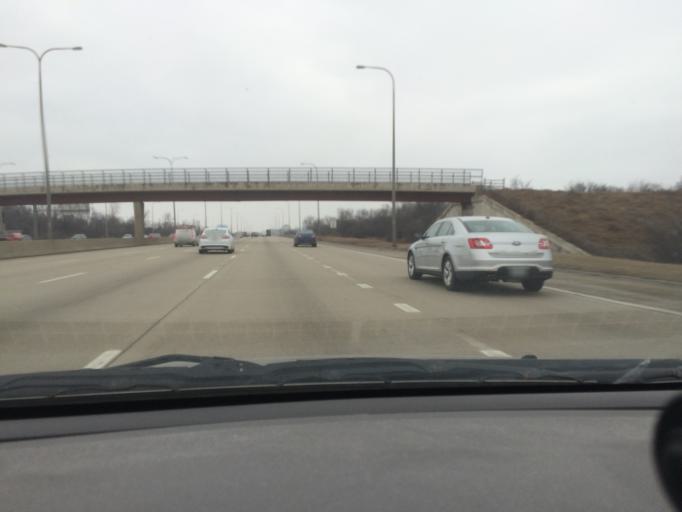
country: US
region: Illinois
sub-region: DuPage County
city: Itasca
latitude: 42.0054
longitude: -88.0272
